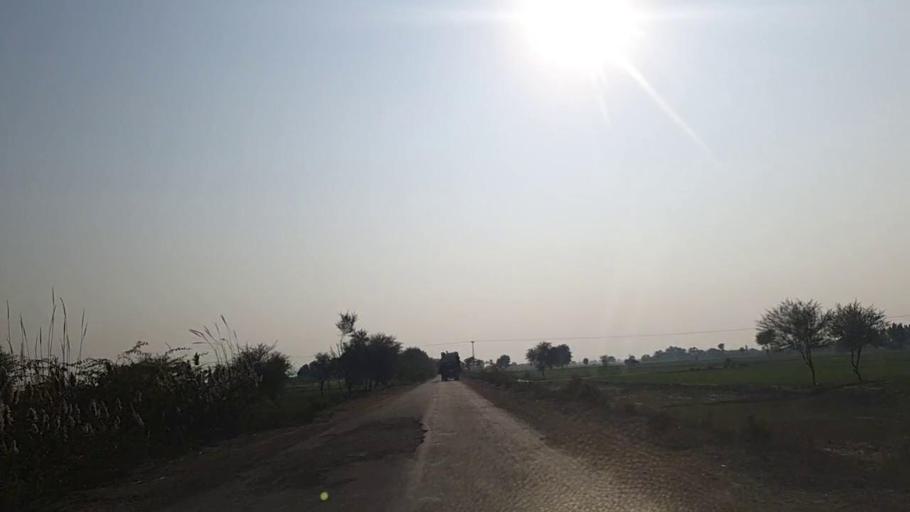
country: PK
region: Sindh
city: Jam Sahib
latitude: 26.2807
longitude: 68.6191
